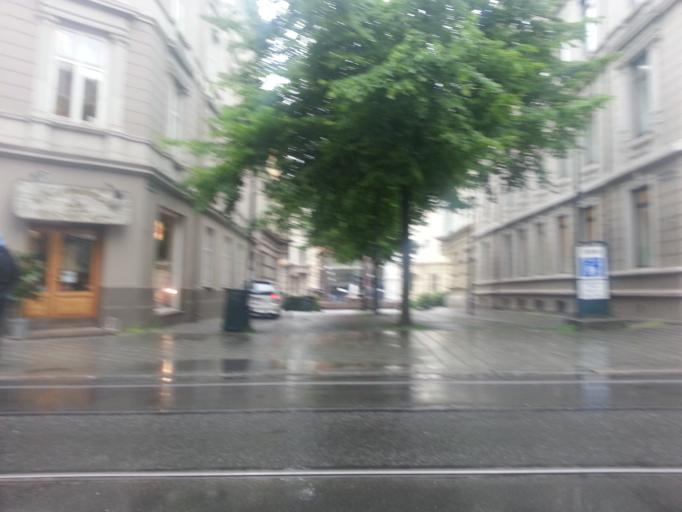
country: NO
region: Oslo
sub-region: Oslo
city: Oslo
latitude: 59.9162
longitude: 10.7397
